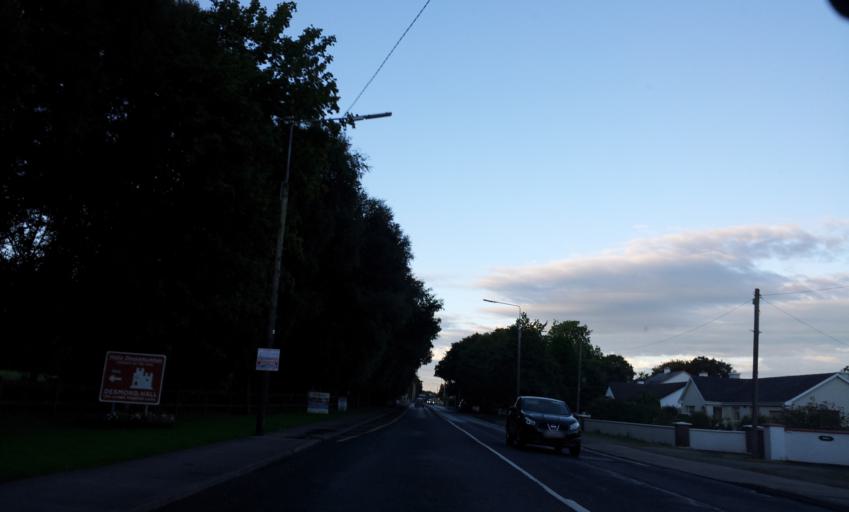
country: IE
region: Munster
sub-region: County Limerick
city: Newcastle West
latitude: 52.4454
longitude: -9.0717
